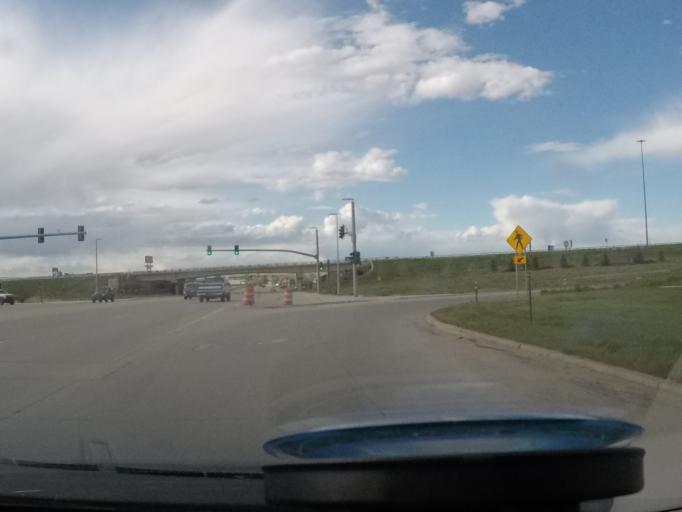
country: US
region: Wyoming
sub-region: Natrona County
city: Evansville
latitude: 42.8523
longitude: -106.2707
